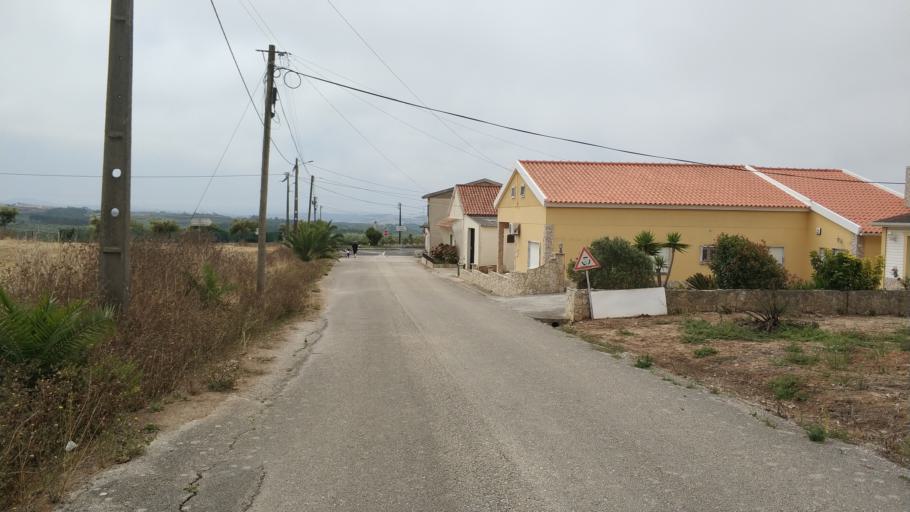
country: PT
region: Lisbon
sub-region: Lourinha
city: Lourinha
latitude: 39.2103
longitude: -9.3211
